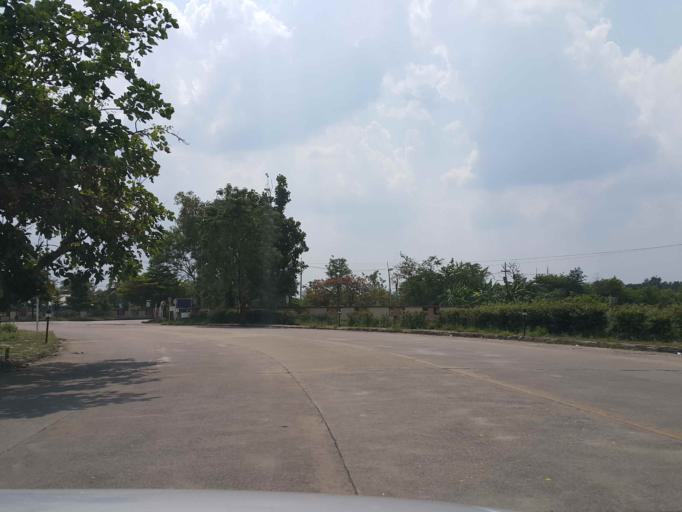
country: TH
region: Chiang Mai
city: Hang Dong
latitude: 18.7020
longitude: 98.9419
